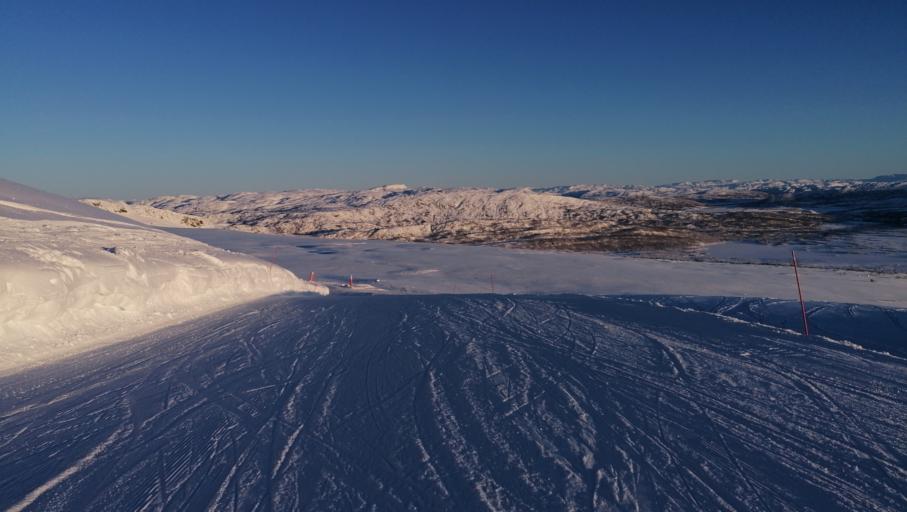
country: NO
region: Aust-Agder
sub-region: Bykle
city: Hovden
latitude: 59.5808
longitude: 7.3316
